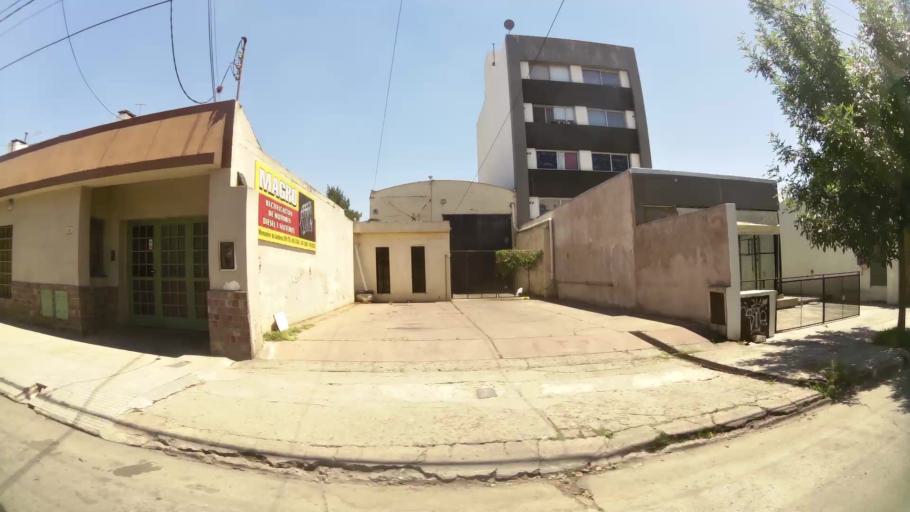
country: AR
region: Cordoba
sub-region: Departamento de Capital
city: Cordoba
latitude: -31.4018
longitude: -64.2165
